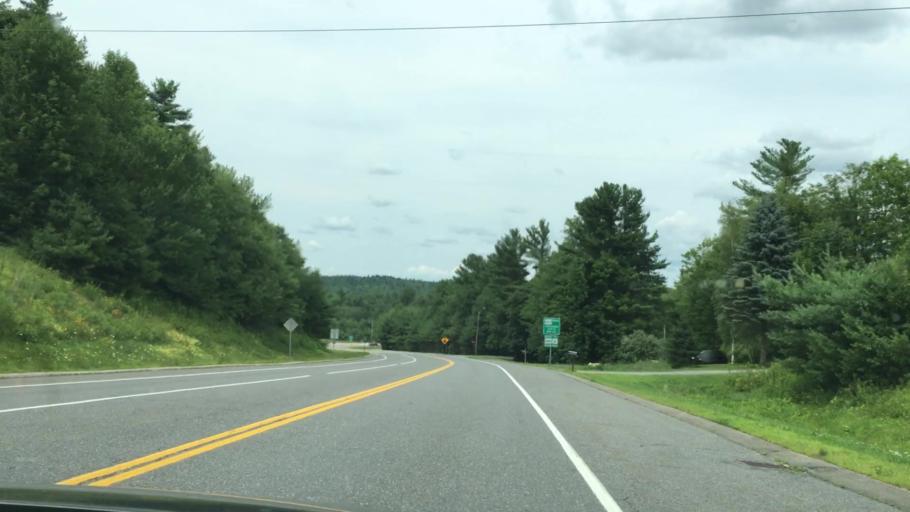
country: US
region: Massachusetts
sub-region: Worcester County
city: Gardner
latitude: 42.6007
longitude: -71.9884
